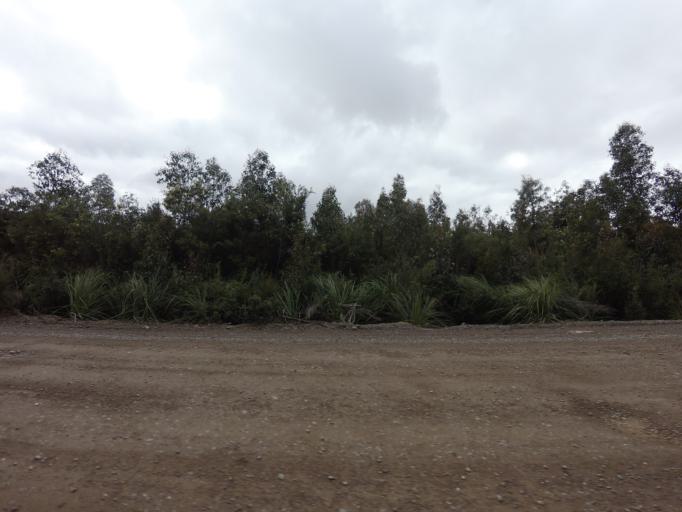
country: AU
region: Tasmania
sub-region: Huon Valley
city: Geeveston
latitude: -43.5107
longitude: 146.8852
